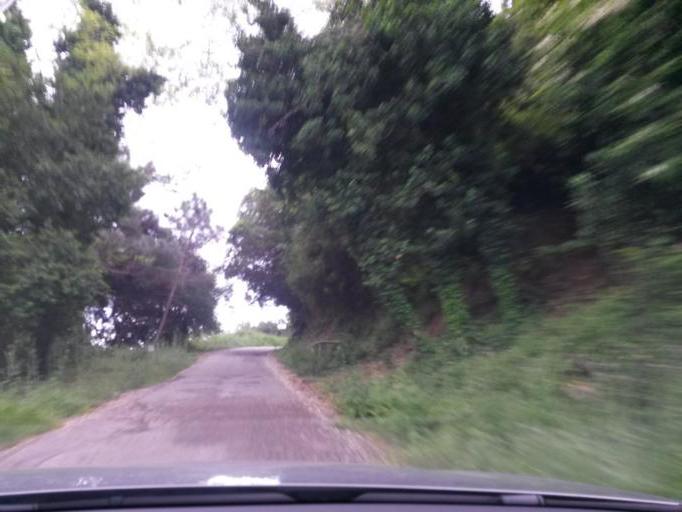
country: IT
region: Tuscany
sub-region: Provincia di Livorno
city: Campo nell'Elba
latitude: 42.7633
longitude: 10.1980
